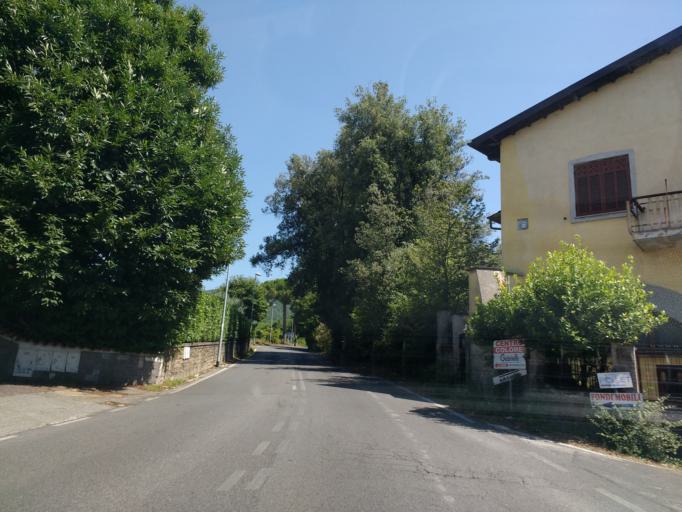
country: IT
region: Latium
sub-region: Citta metropolitana di Roma Capitale
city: Rocca di Papa
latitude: 41.7724
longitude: 12.7003
